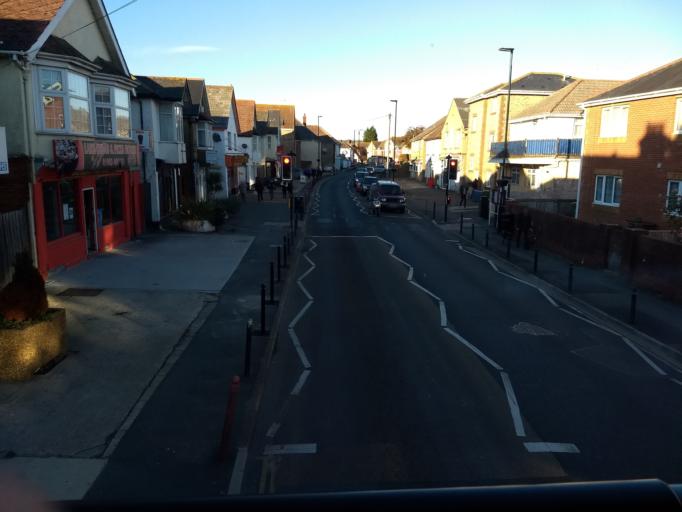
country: GB
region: England
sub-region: Isle of Wight
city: Sandown
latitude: 50.6486
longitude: -1.1683
